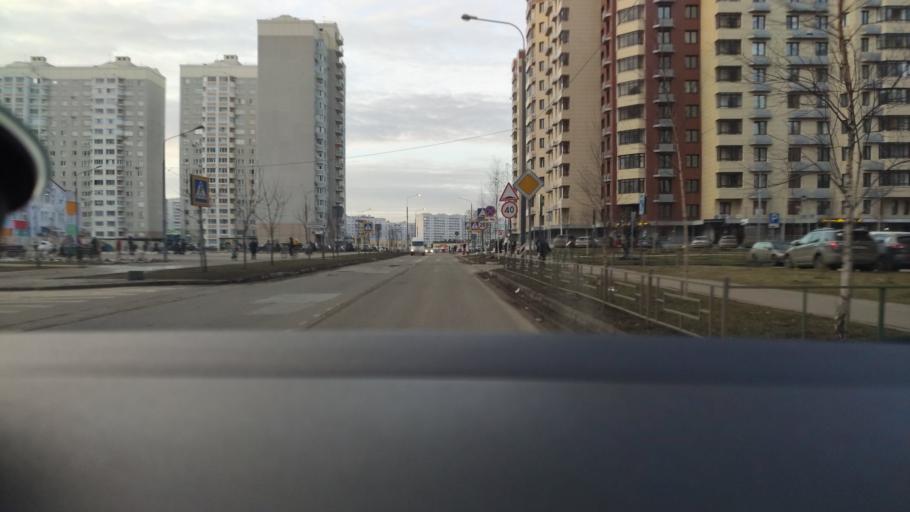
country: RU
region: Moskovskaya
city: Vidnoye
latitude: 55.5388
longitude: 37.7220
